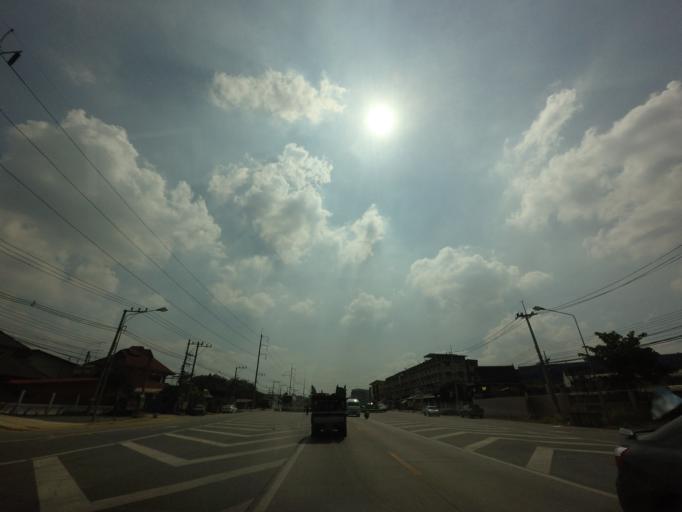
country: TH
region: Nakhon Pathom
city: Sam Phran
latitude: 13.7508
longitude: 100.2302
